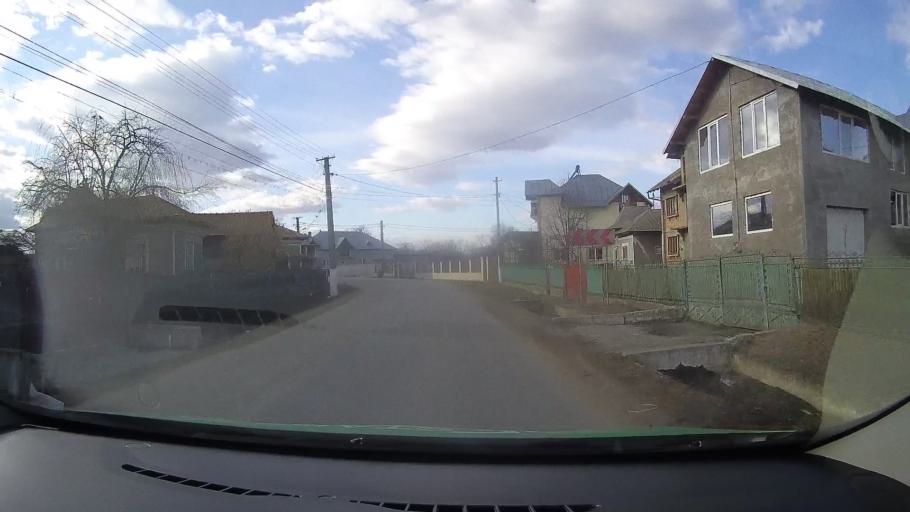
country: RO
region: Dambovita
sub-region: Comuna Ulmi
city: Ulmi
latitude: 44.8803
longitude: 25.5154
